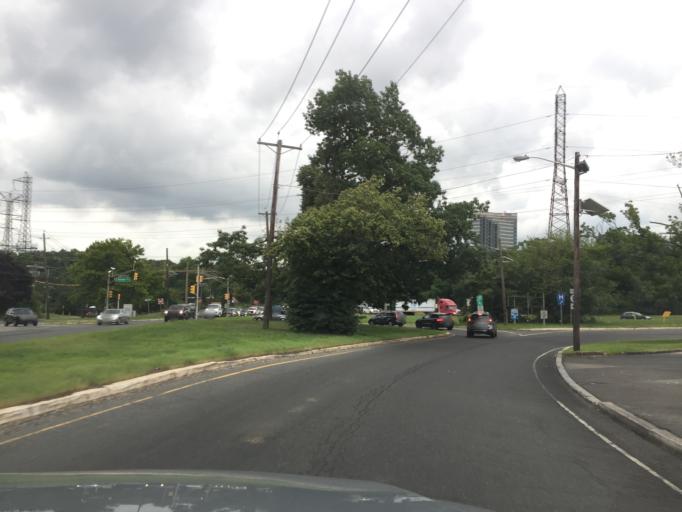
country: US
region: New Jersey
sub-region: Middlesex County
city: Highland Park
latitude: 40.4839
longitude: -74.4161
